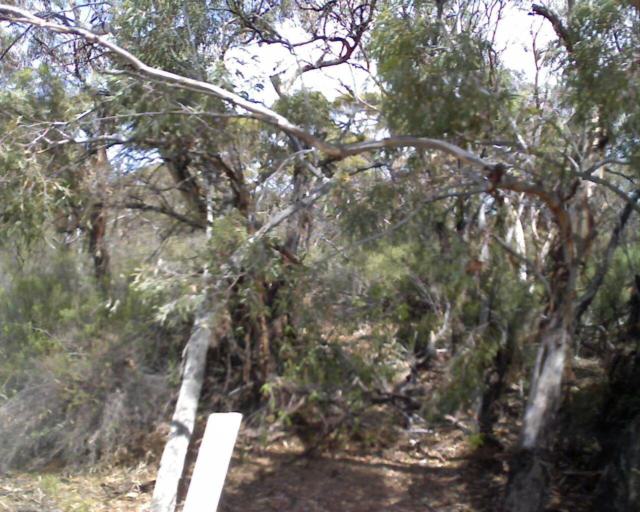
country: AU
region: Western Australia
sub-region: Kalgoorlie/Boulder
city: Stoneville
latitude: -31.2045
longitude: 121.6622
